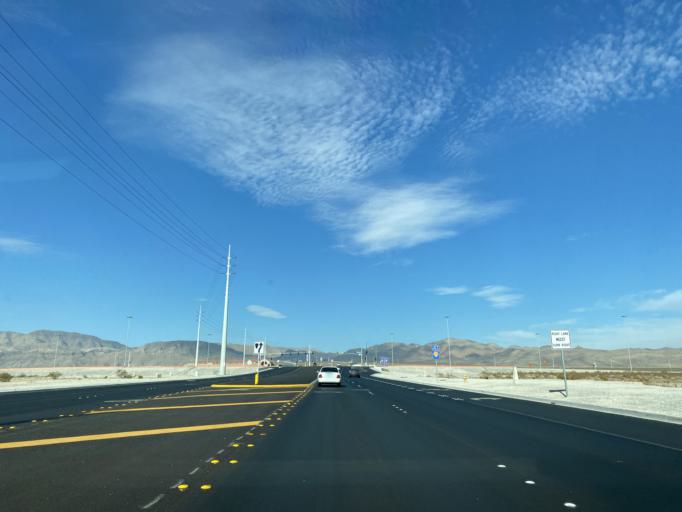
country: US
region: Nevada
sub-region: Clark County
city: Nellis Air Force Base
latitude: 36.2866
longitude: -115.0798
